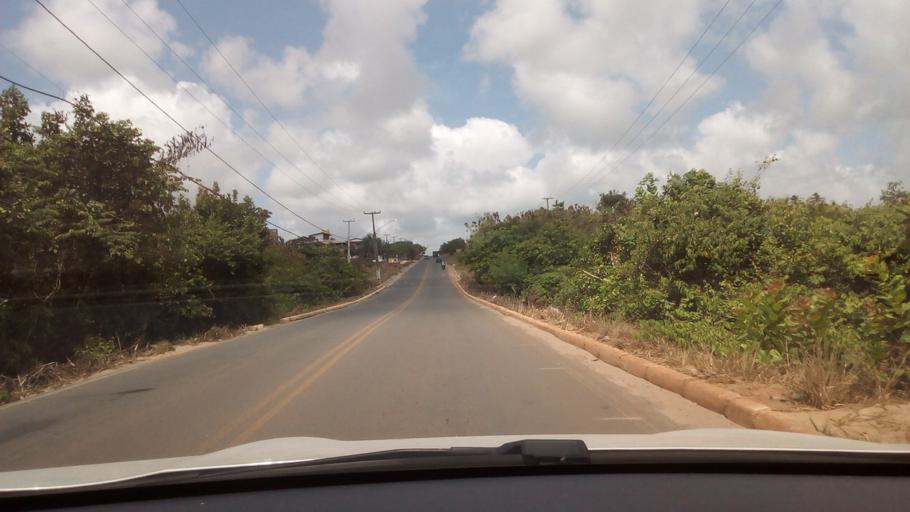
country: BR
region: Paraiba
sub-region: Conde
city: Conde
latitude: -7.2777
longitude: -34.8024
